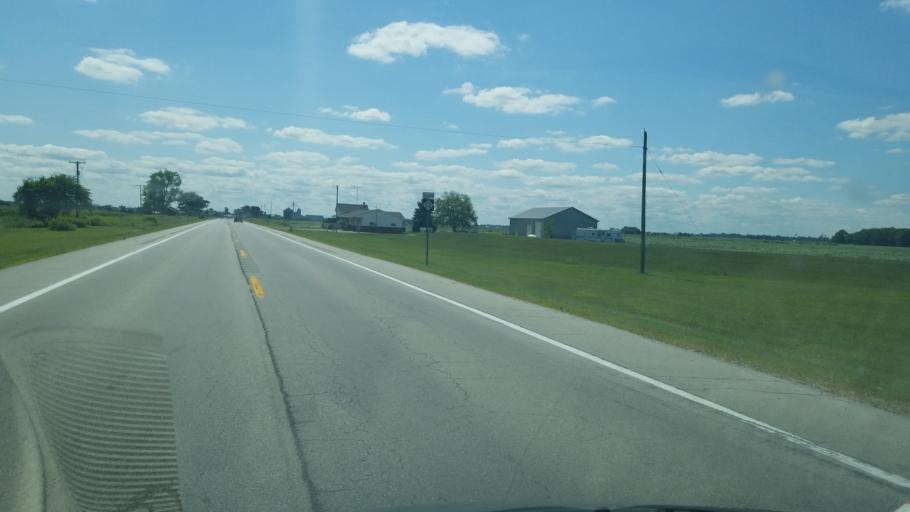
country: US
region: Ohio
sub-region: Fulton County
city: Delta
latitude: 41.7278
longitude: -84.0373
